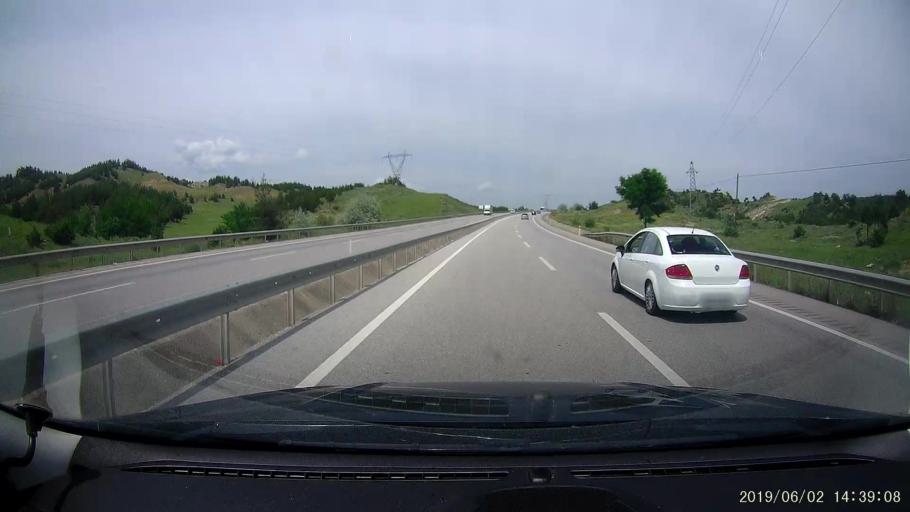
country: TR
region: Corum
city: Hacihamza
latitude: 41.0664
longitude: 34.2928
